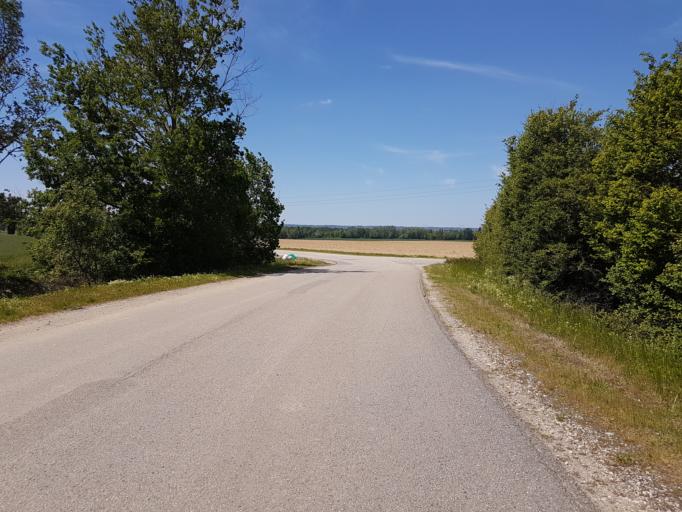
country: FR
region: Rhone-Alpes
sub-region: Departement du Rhone
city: Jons
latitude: 45.7872
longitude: 5.0780
